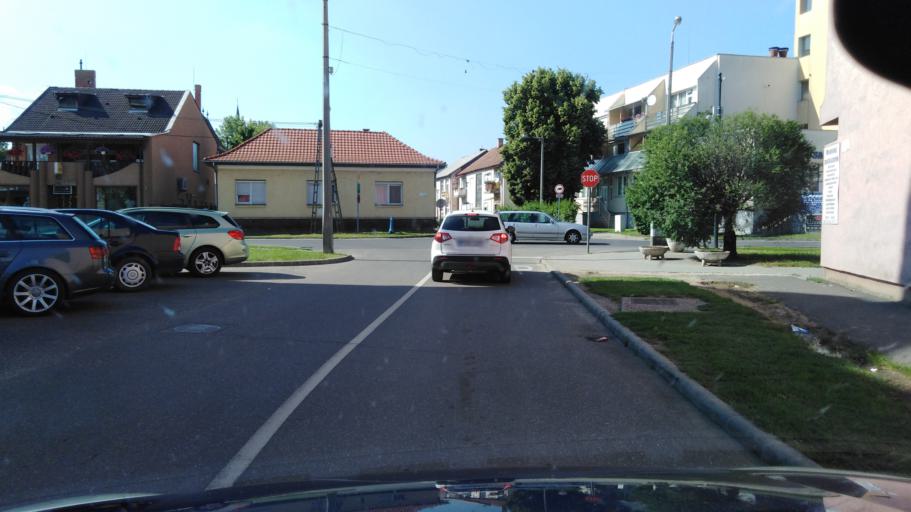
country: HU
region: Szabolcs-Szatmar-Bereg
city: Nyirbator
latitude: 47.8352
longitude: 22.1304
